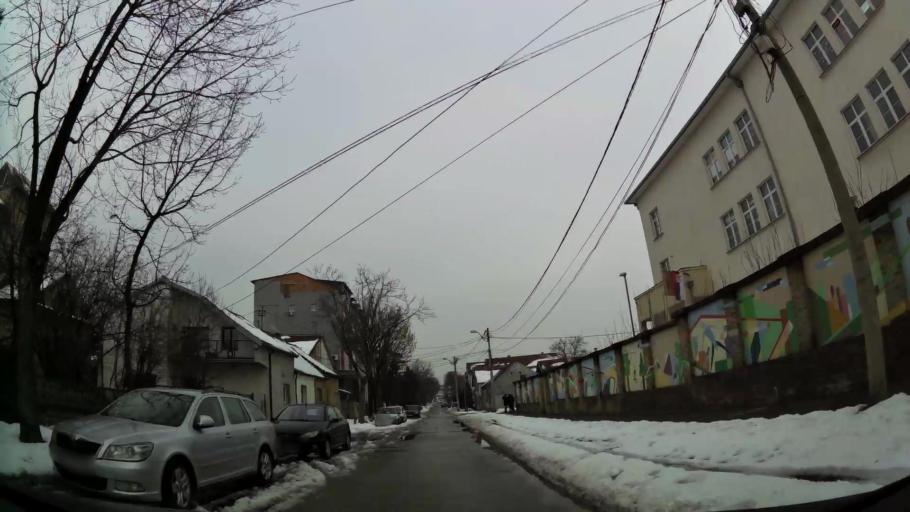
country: RS
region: Central Serbia
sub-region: Belgrade
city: Zemun
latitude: 44.8533
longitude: 20.3845
